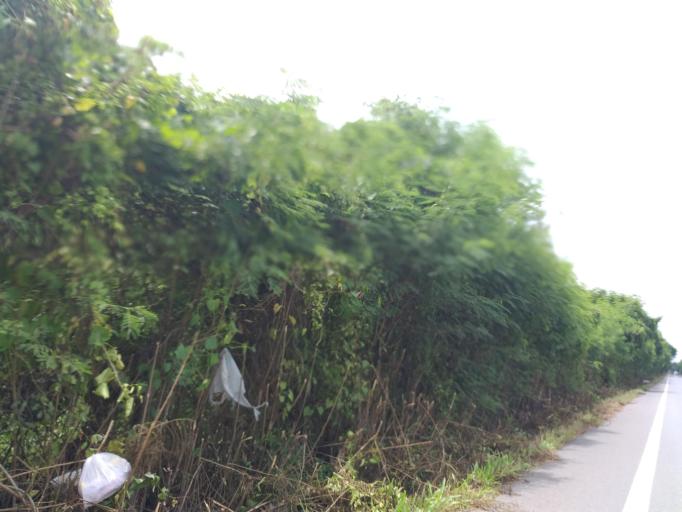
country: TH
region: Pathum Thani
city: Nong Suea
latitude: 14.0624
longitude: 100.8715
